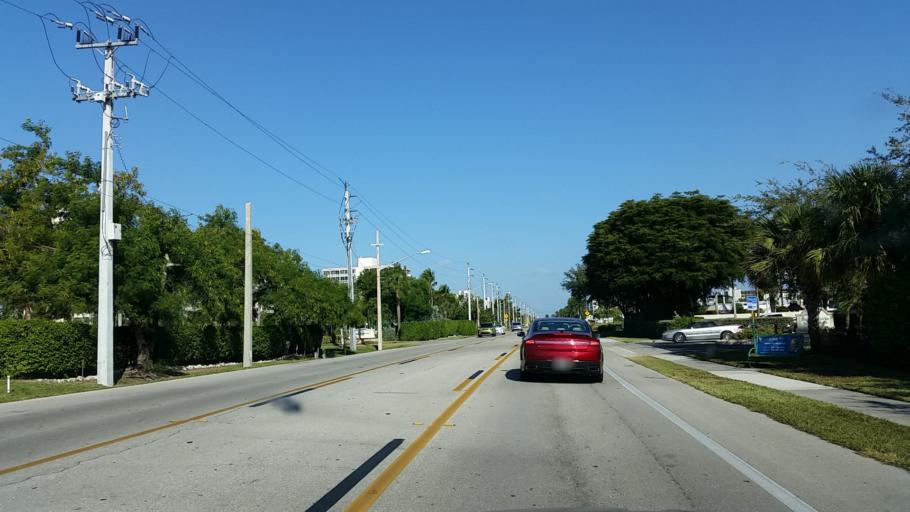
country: US
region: Florida
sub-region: Lee County
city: Fort Myers Beach
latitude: 26.4112
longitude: -81.8993
